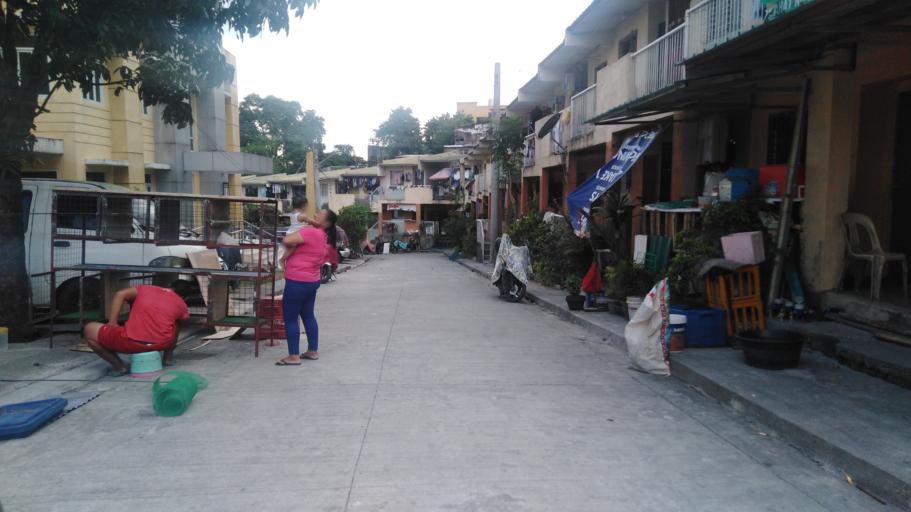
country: PH
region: Calabarzon
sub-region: Province of Rizal
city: San Mateo
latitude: 14.7130
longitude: 121.0951
